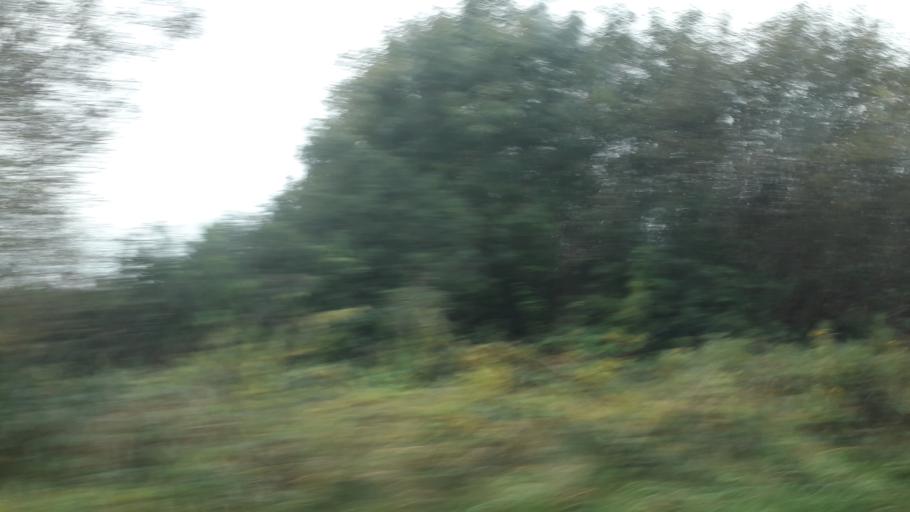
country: IE
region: Leinster
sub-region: An Longfort
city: Lanesborough
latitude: 53.7504
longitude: -7.9535
